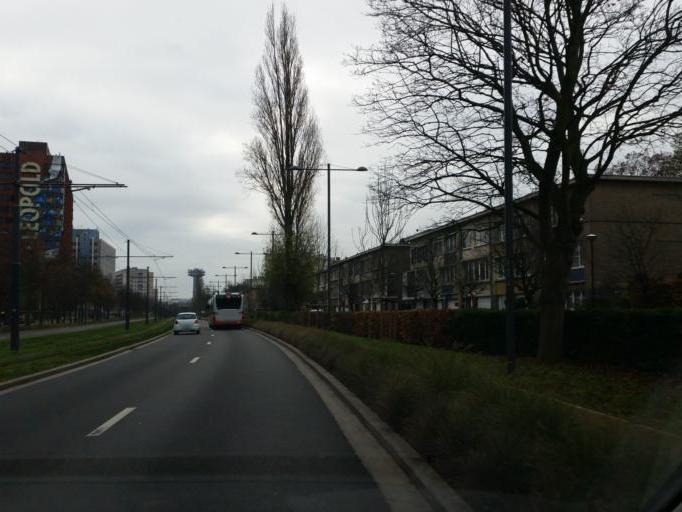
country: BE
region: Flanders
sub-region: Provincie Vlaams-Brabant
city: Diegem
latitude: 50.8662
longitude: 4.4023
